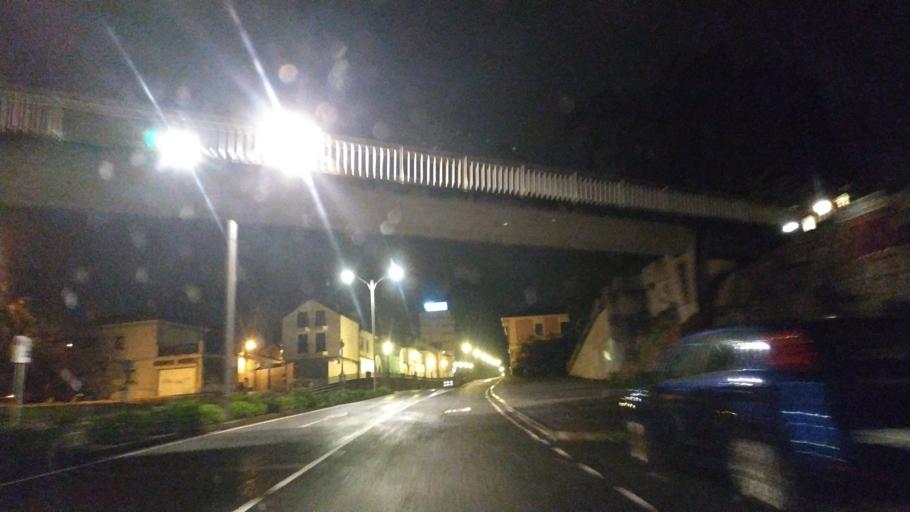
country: ES
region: Galicia
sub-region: Provincia da Coruna
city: A Coruna
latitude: 43.3612
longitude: -8.4110
